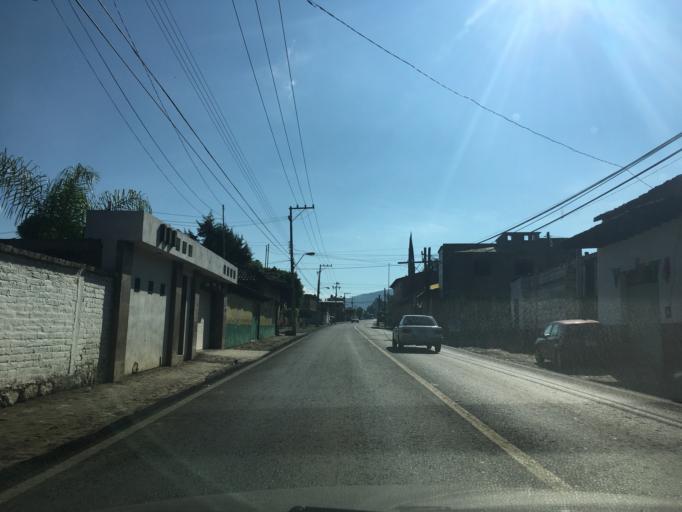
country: MX
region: Mexico
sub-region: Chalco
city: Santo Tomas
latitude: 19.8454
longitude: -102.0990
